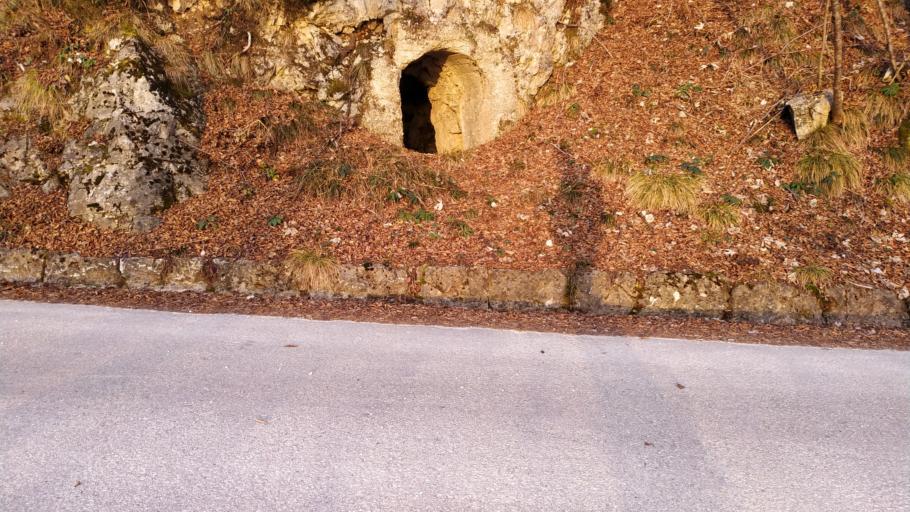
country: IT
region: Veneto
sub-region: Provincia di Vicenza
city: Velo d'Astico
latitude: 45.7663
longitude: 11.3682
